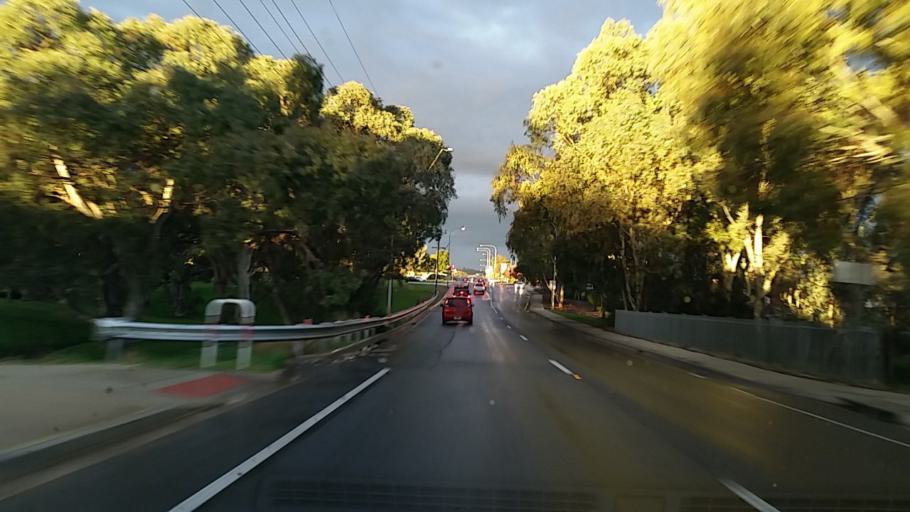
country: AU
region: South Australia
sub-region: Tea Tree Gully
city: Modbury
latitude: -34.8282
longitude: 138.6854
